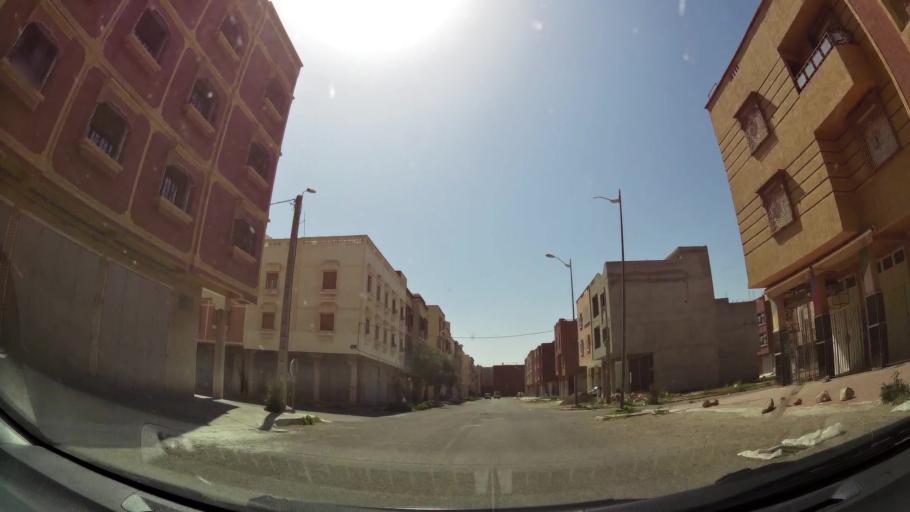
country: MA
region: Souss-Massa-Draa
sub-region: Inezgane-Ait Mellou
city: Inezgane
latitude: 30.3306
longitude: -9.5081
